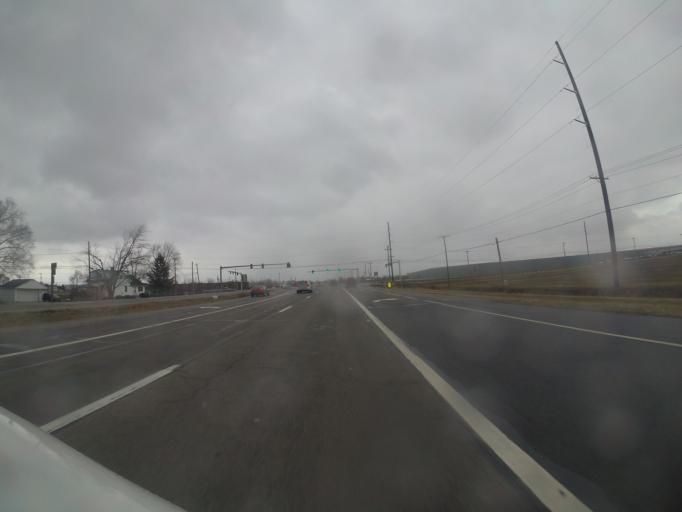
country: US
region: Ohio
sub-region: Wood County
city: Walbridge
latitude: 41.5637
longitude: -83.5291
